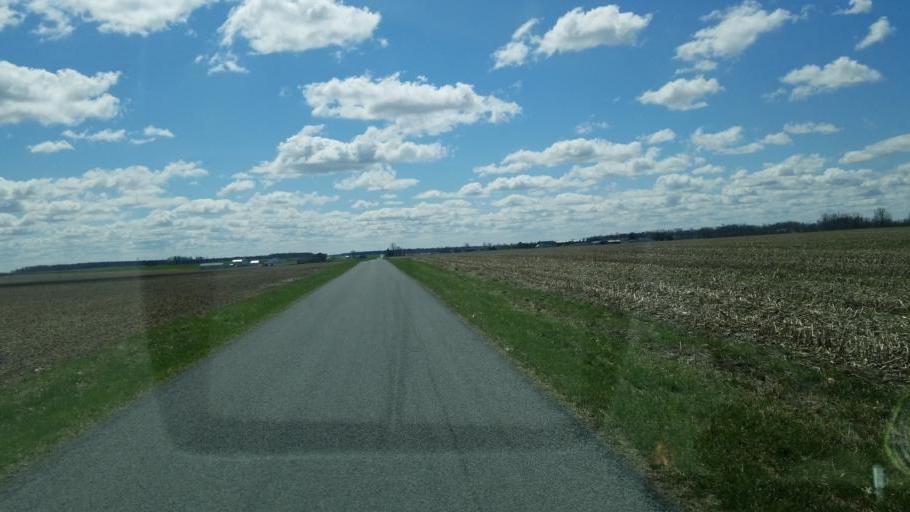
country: US
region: Ohio
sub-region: Seneca County
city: Fostoria
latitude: 41.0741
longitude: -83.5146
